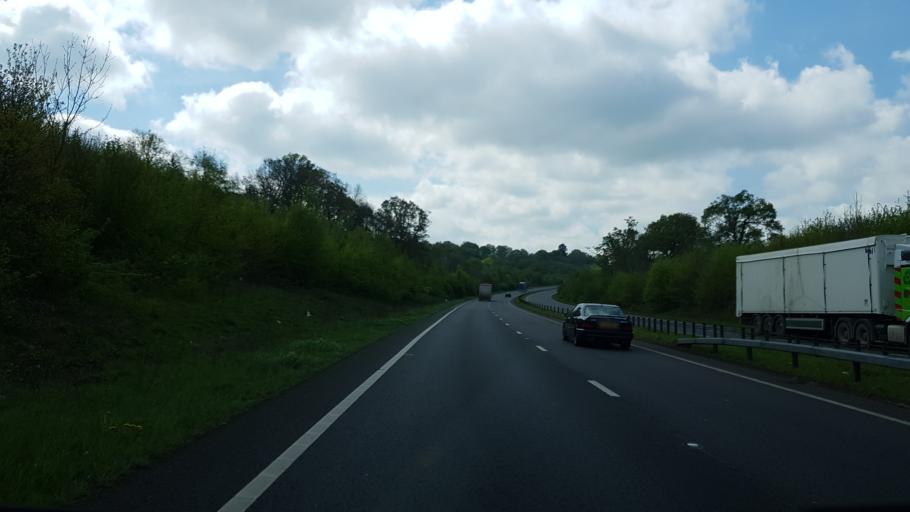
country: GB
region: England
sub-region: East Sussex
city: Wadhurst
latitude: 51.0994
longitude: 0.4036
